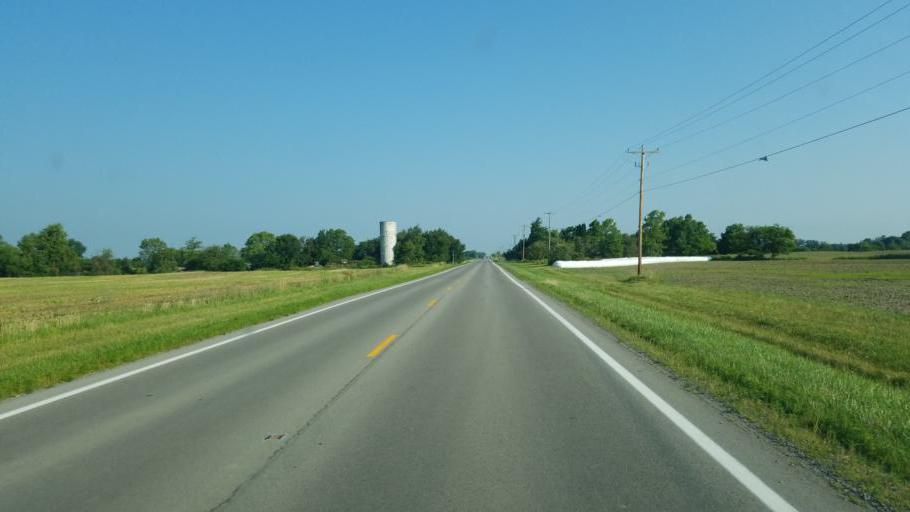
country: US
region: Ohio
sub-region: Hardin County
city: Kenton
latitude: 40.5558
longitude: -83.5387
